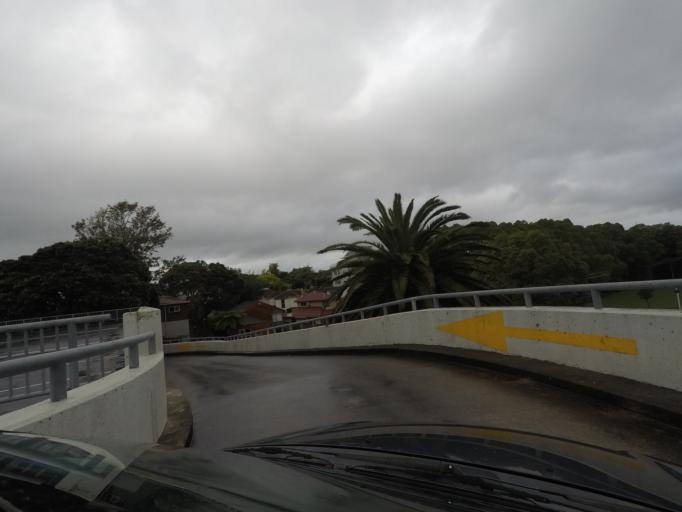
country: NZ
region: Auckland
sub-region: Auckland
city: Auckland
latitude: -36.8829
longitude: 174.7356
